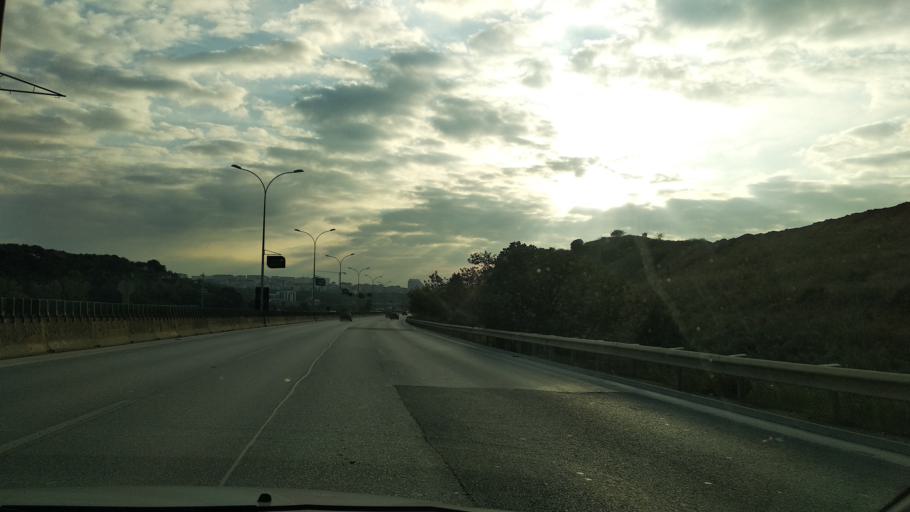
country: TR
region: Istanbul
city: Icmeler
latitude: 40.8852
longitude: 29.3220
